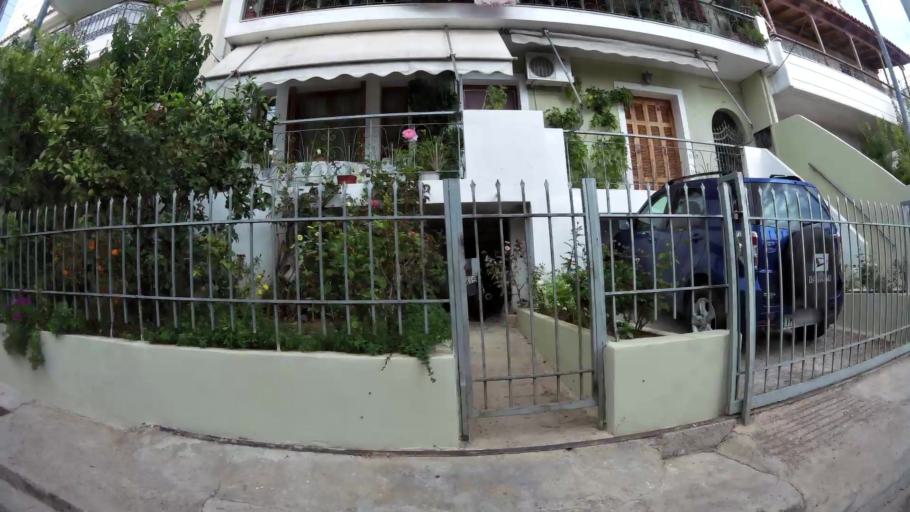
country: GR
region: Attica
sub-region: Nomarchia Dytikis Attikis
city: Zefyri
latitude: 38.0569
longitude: 23.7218
